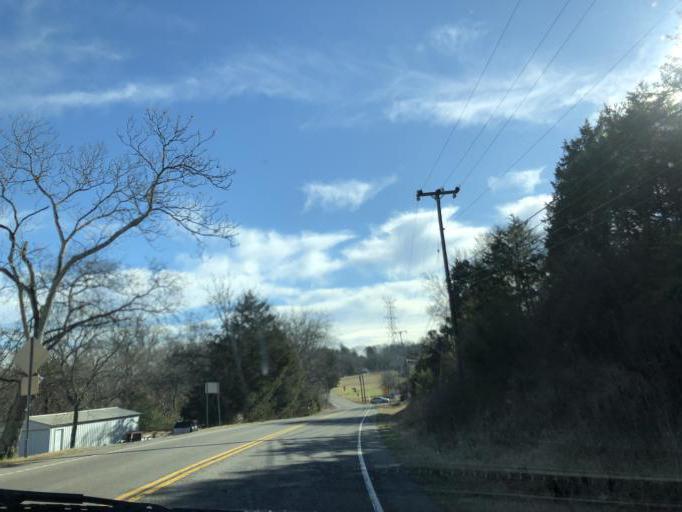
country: US
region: Tennessee
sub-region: Wilson County
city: Green Hill
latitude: 36.1734
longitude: -86.5716
